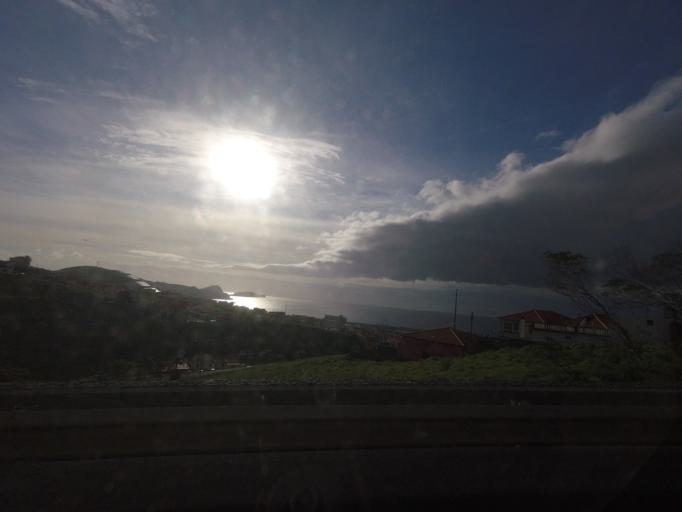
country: PT
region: Madeira
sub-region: Machico
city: Canical
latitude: 32.7432
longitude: -16.7453
